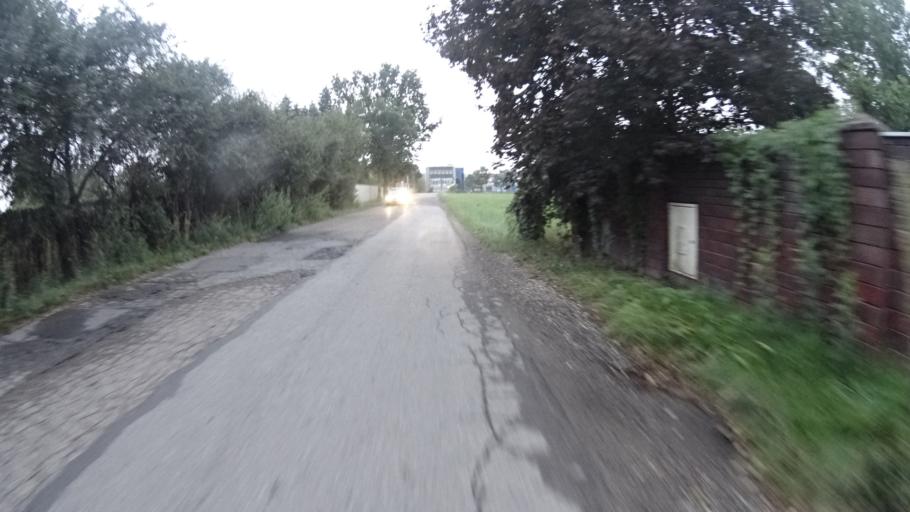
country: PL
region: Masovian Voivodeship
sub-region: Warszawa
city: Ursus
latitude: 52.2180
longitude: 20.8864
